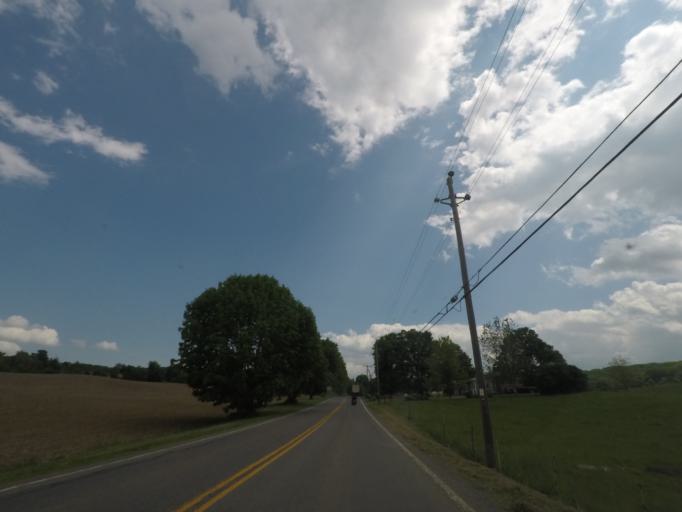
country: US
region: New York
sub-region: Dutchess County
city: Pine Plains
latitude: 42.0307
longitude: -73.6112
